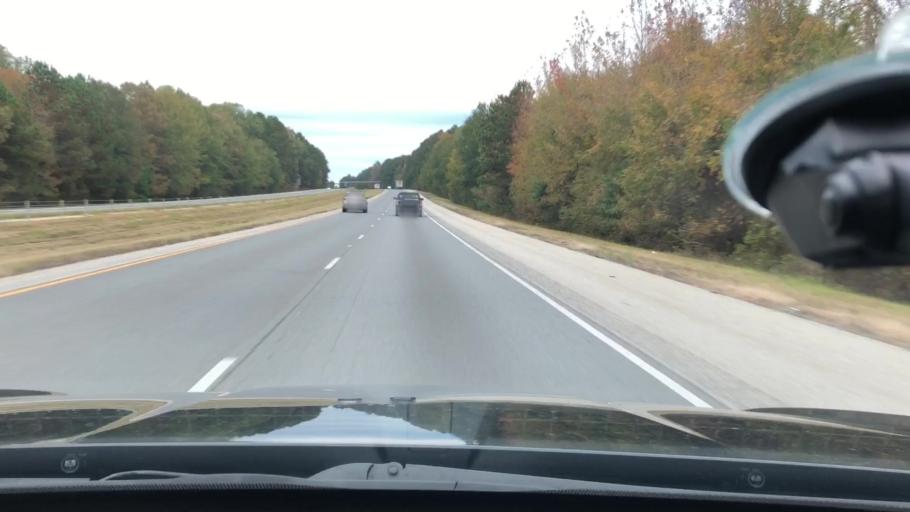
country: US
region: Arkansas
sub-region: Clark County
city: Arkadelphia
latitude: 34.1365
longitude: -93.0832
